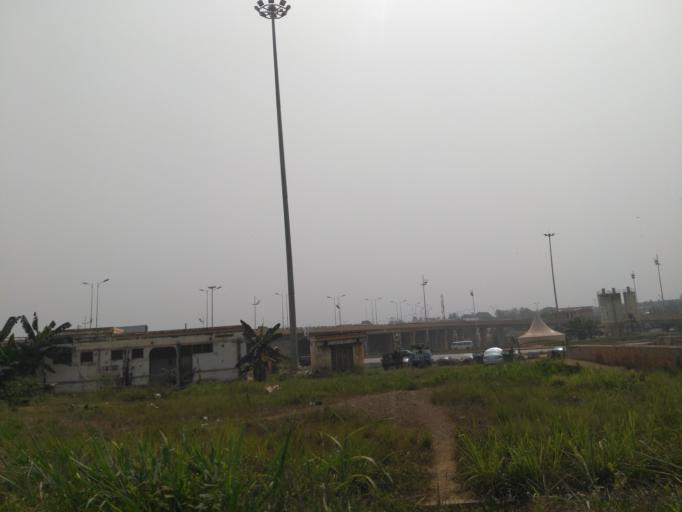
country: GH
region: Ashanti
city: Kumasi
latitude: 6.7013
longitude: -1.6456
